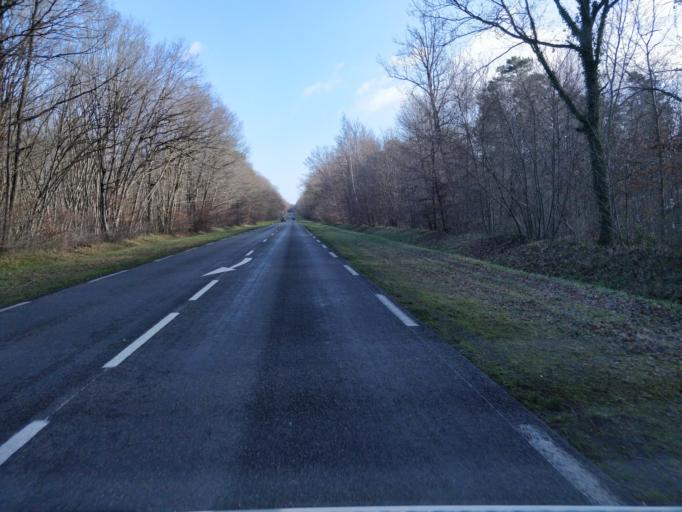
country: FR
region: Ile-de-France
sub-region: Departement de Seine-et-Marne
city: Souppes-sur-Loing
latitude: 48.2443
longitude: 2.7884
